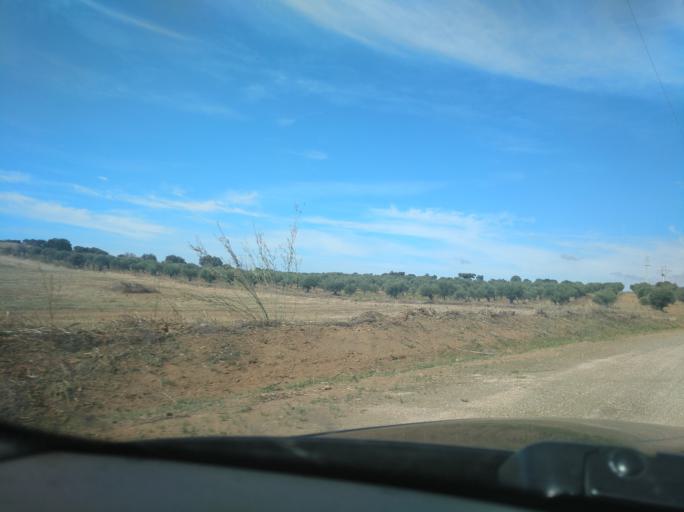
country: PT
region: Portalegre
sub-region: Campo Maior
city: Campo Maior
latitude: 39.0479
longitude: -7.0501
